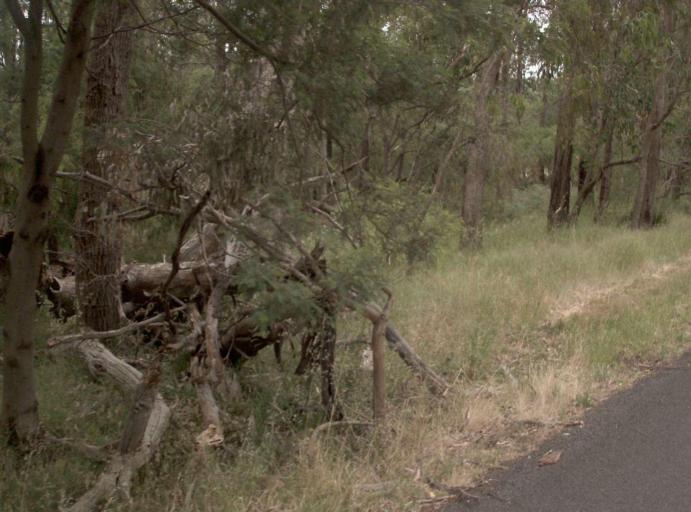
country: AU
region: Victoria
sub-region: Latrobe
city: Morwell
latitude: -38.2871
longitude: 146.3103
